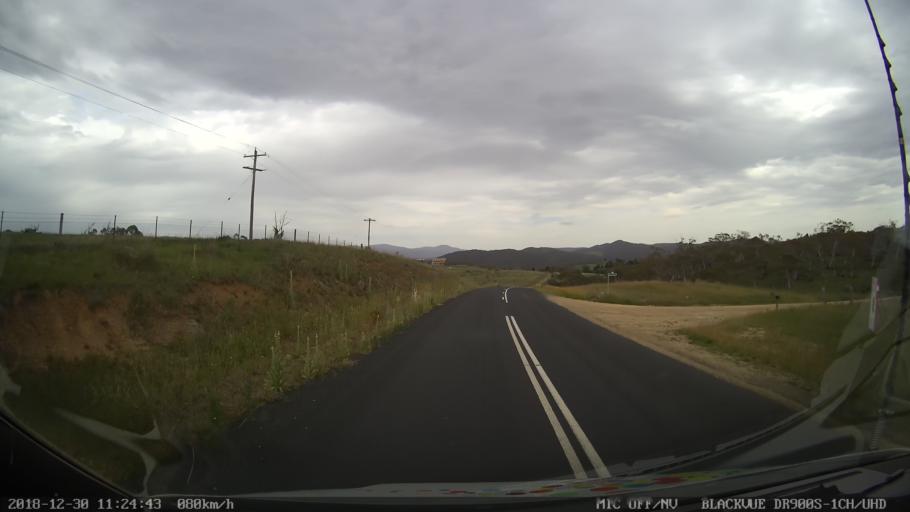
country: AU
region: New South Wales
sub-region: Snowy River
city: Jindabyne
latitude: -36.4805
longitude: 148.6482
